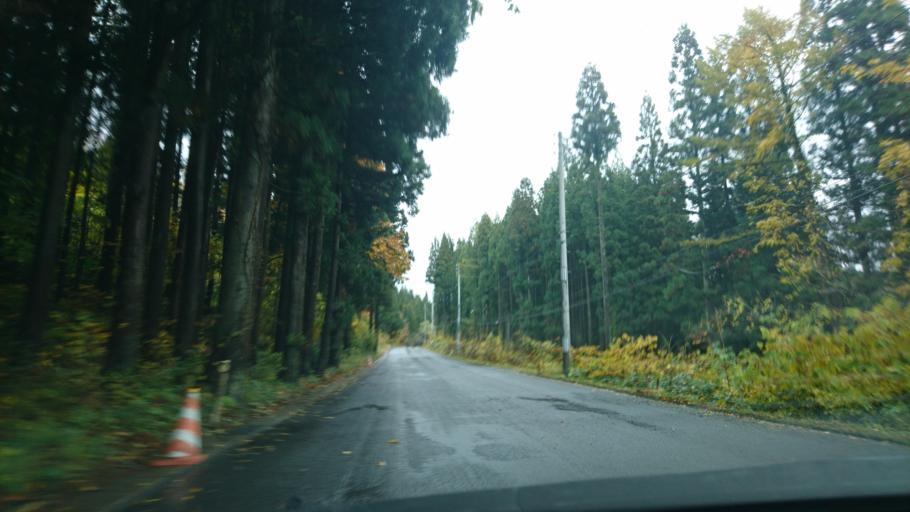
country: JP
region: Iwate
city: Shizukuishi
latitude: 39.4995
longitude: 140.8169
